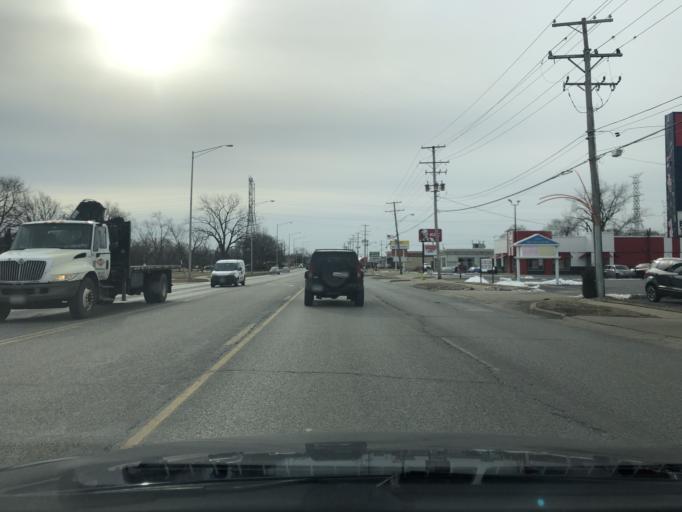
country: US
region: Illinois
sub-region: DuPage County
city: Elmhurst
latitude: 41.9271
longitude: -87.9399
